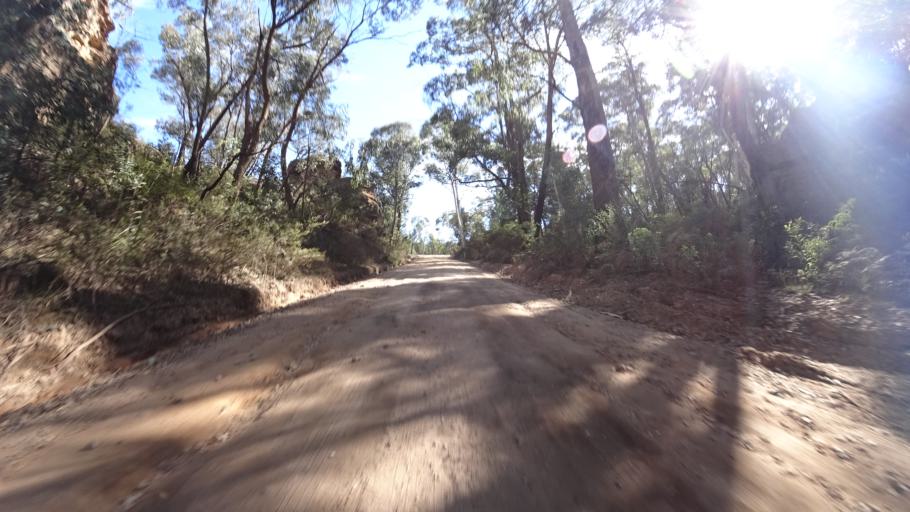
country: AU
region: New South Wales
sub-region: Lithgow
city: Lithgow
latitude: -33.4449
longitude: 150.1801
